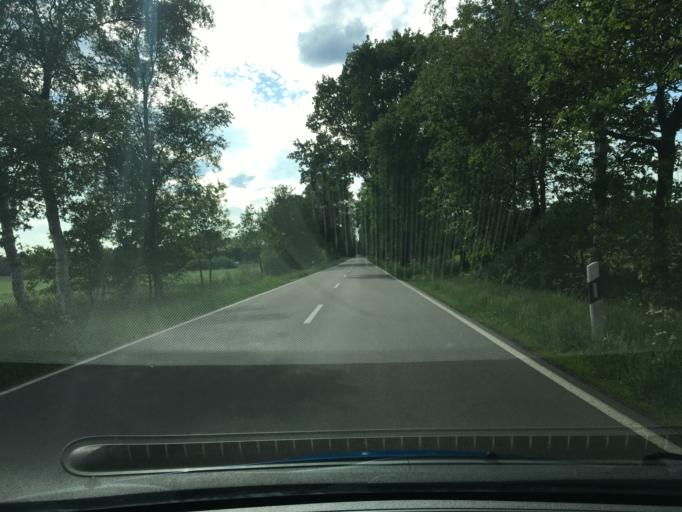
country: DE
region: Lower Saxony
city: Wistedt
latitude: 53.2731
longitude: 9.6459
